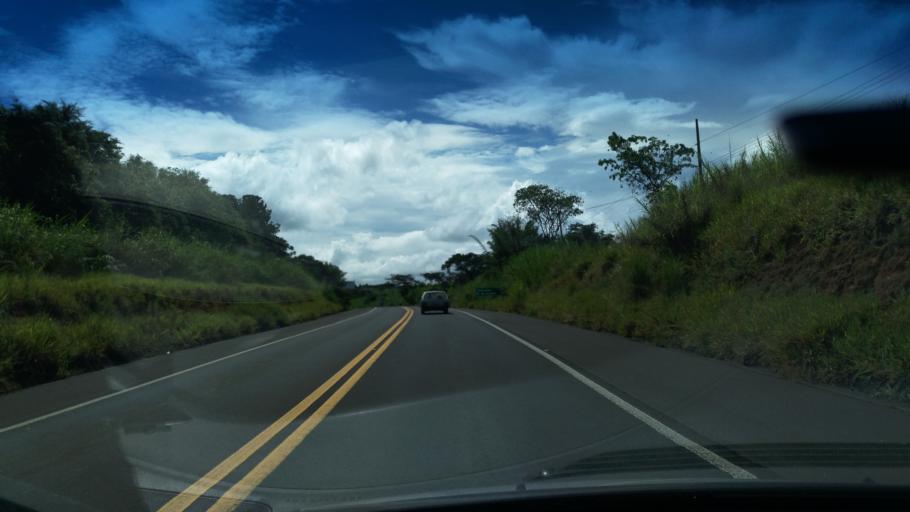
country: BR
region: Sao Paulo
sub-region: Santo Antonio Do Jardim
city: Espirito Santo do Pinhal
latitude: -22.1614
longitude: -46.7315
